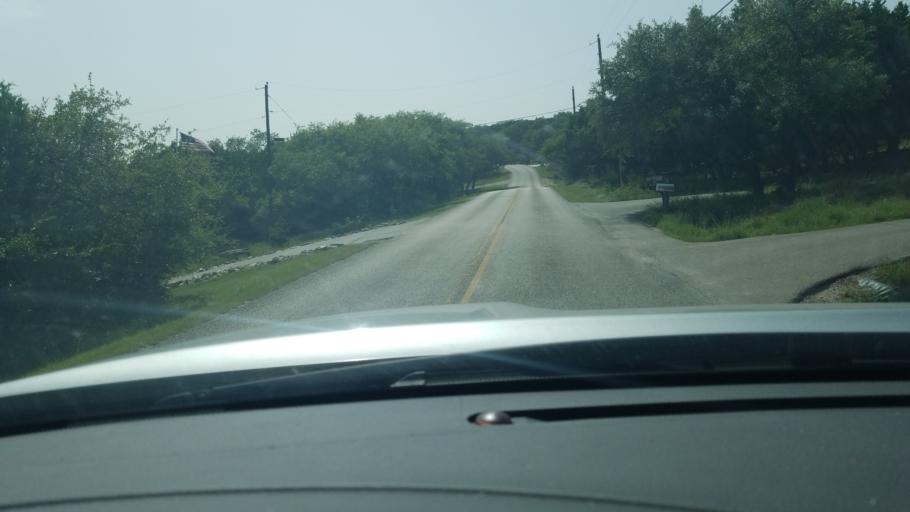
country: US
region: Texas
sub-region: Comal County
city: Bulverde
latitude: 29.7932
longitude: -98.4362
